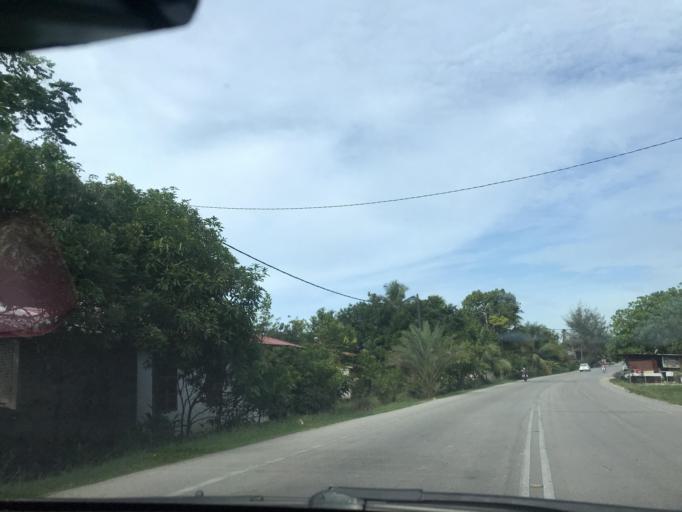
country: MY
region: Kelantan
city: Kota Bharu
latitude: 6.1386
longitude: 102.2074
